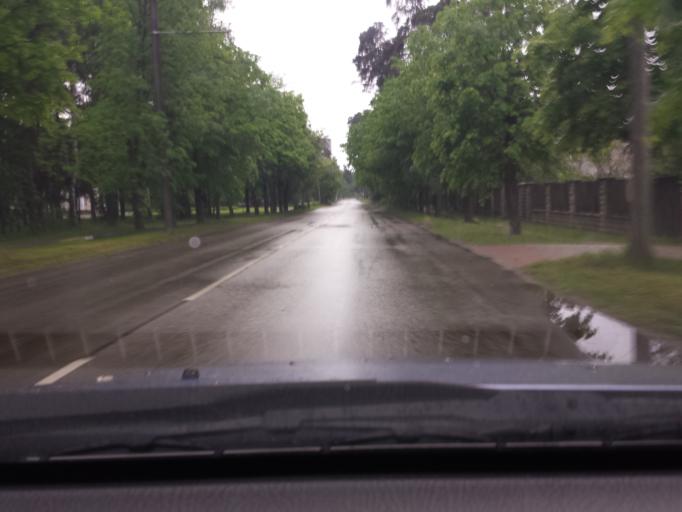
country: LV
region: Riga
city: Bolderaja
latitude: 57.0460
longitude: 24.0932
